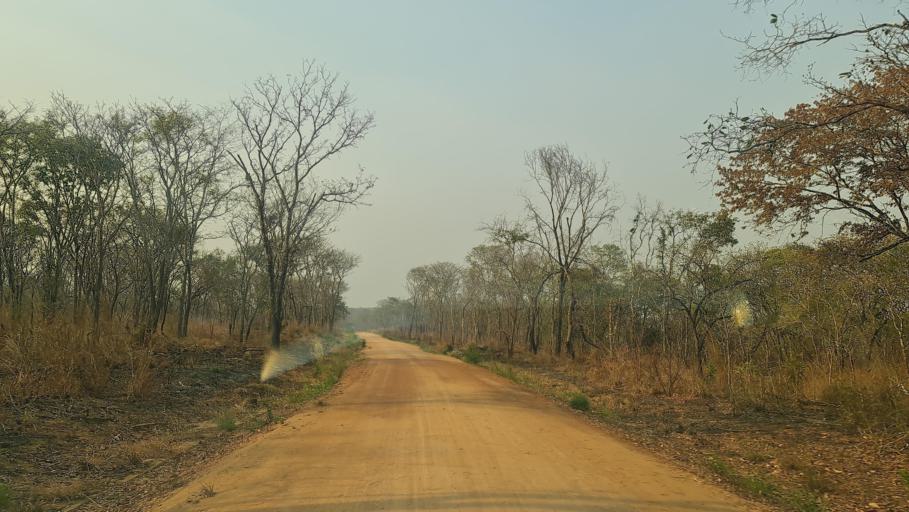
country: MZ
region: Zambezia
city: Quelimane
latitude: -17.1470
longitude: 37.1353
